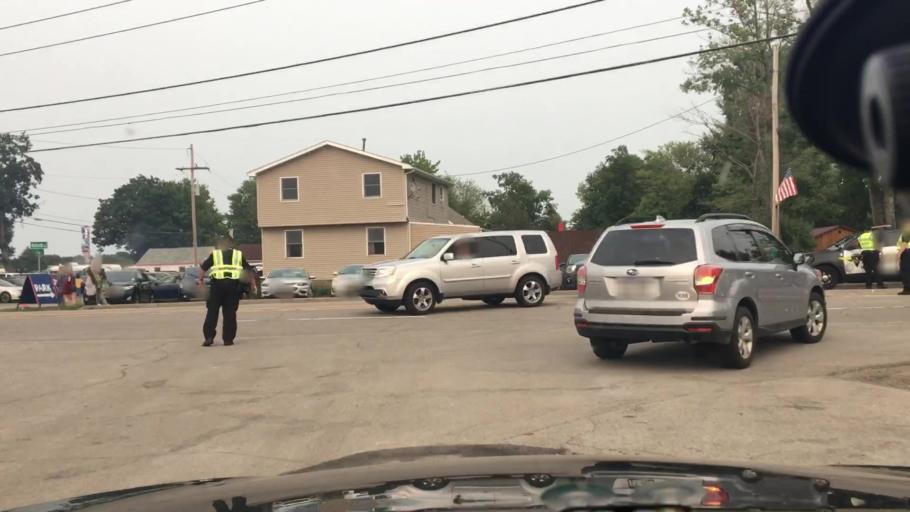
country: US
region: New York
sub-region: Erie County
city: Blasdell
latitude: 42.7708
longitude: -78.7908
